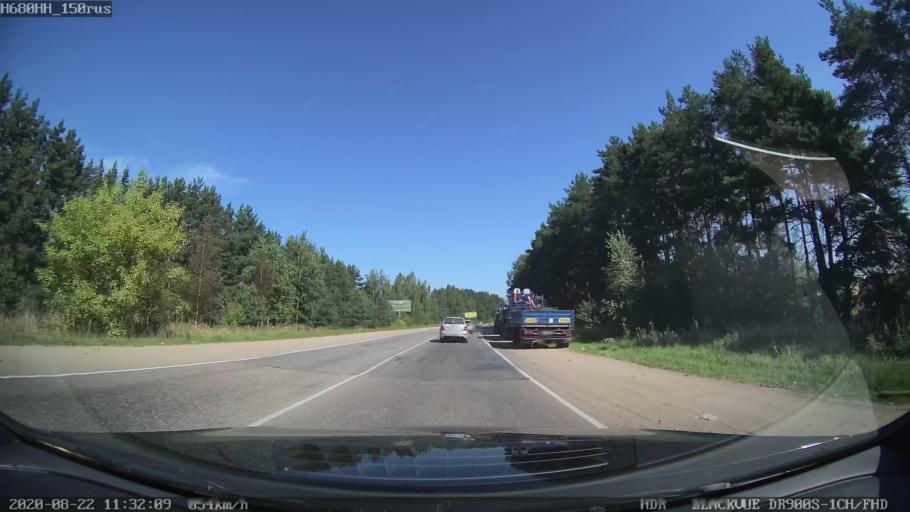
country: RU
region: Tverskaya
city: Tver
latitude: 56.9056
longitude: 35.9338
